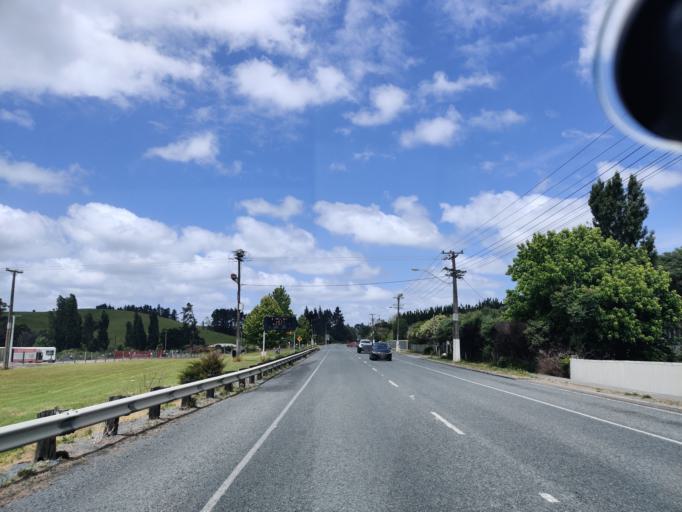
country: NZ
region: Auckland
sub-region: Auckland
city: Wellsford
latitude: -36.2565
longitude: 174.5095
